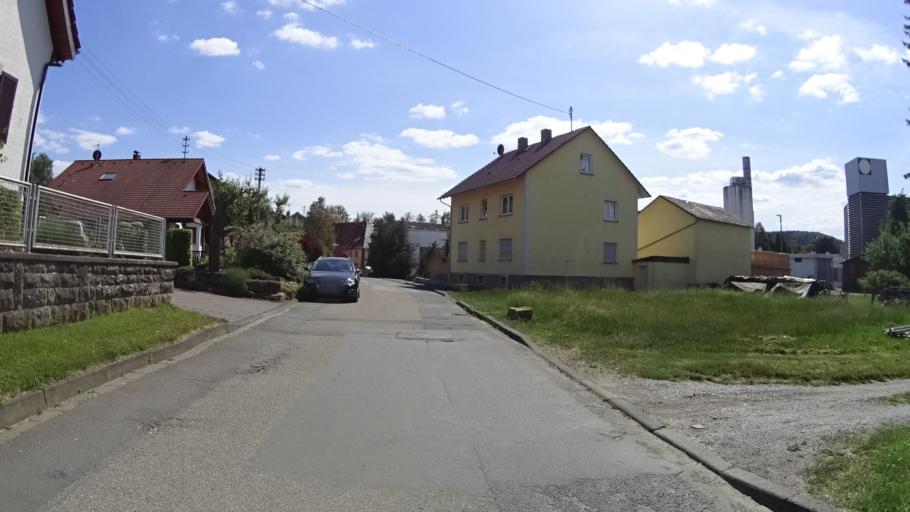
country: DE
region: Baden-Wuerttemberg
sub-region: Karlsruhe Region
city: Hardheim
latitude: 49.6060
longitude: 9.4773
